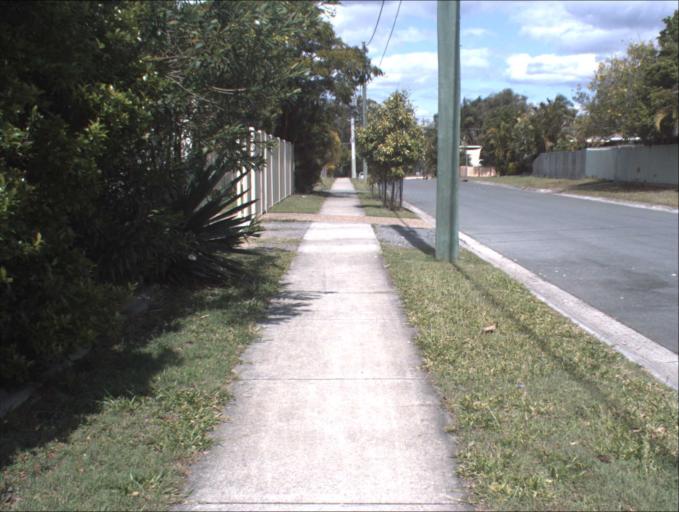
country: AU
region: Queensland
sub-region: Logan
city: Logan City
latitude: -27.6725
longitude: 153.0878
